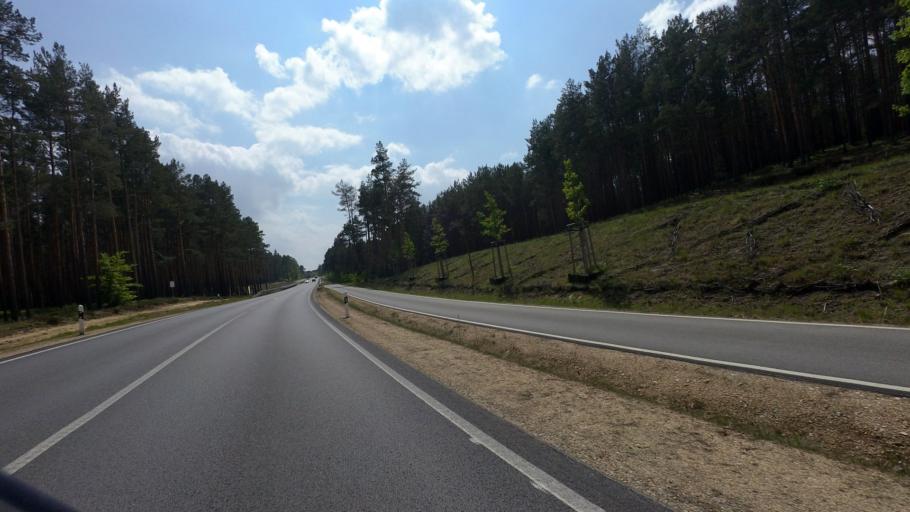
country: DE
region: Saxony
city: Rietschen
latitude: 51.4216
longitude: 14.7895
